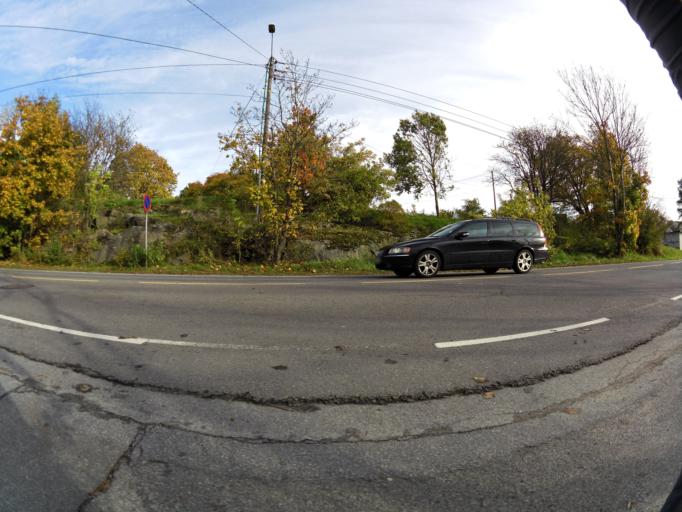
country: NO
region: Ostfold
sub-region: Fredrikstad
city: Fredrikstad
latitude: 59.2223
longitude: 10.9306
